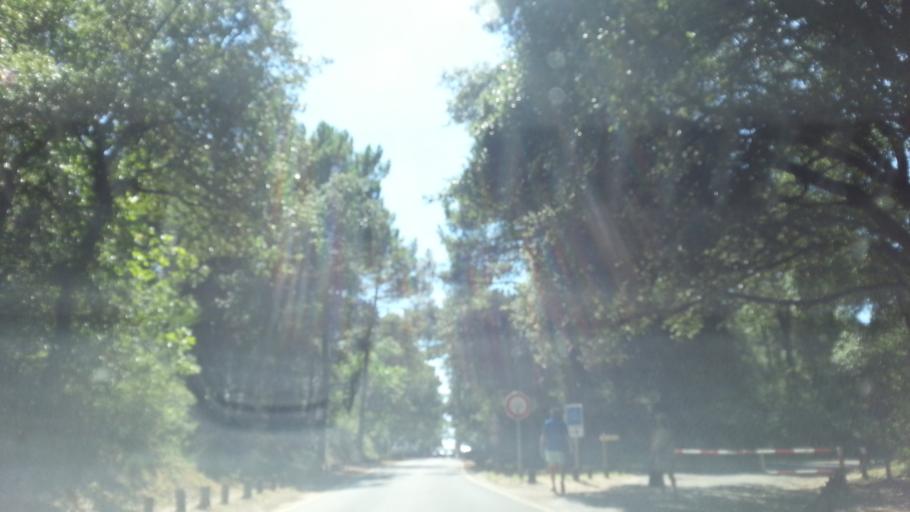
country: FR
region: Poitou-Charentes
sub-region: Departement de la Charente-Maritime
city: Dolus-d'Oleron
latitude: 45.8804
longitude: -1.2571
